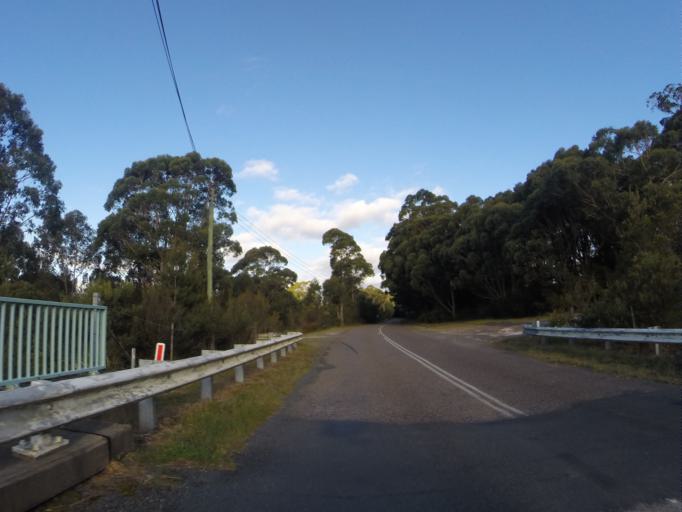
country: AU
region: New South Wales
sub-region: Shoalhaven Shire
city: Kangaroo Valley
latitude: -34.6561
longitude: 150.4913
